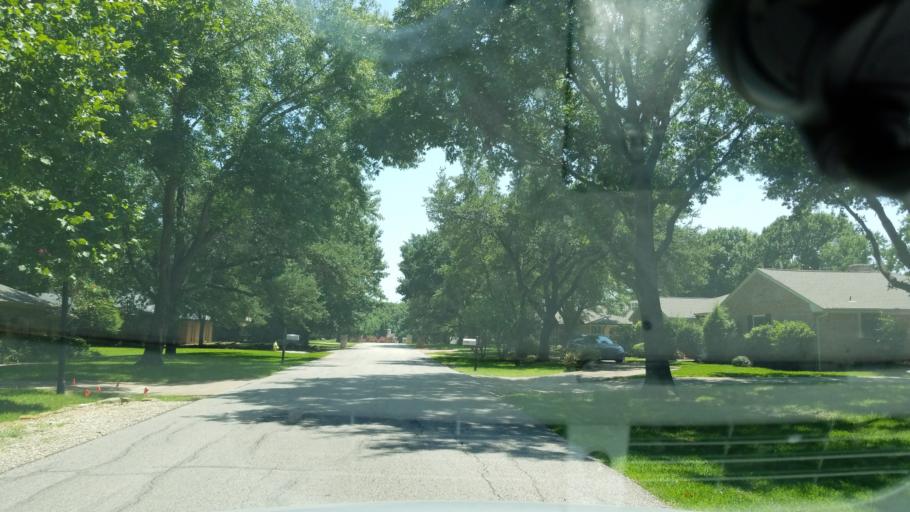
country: US
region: Texas
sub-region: Dallas County
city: Coppell
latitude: 32.9583
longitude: -96.9878
